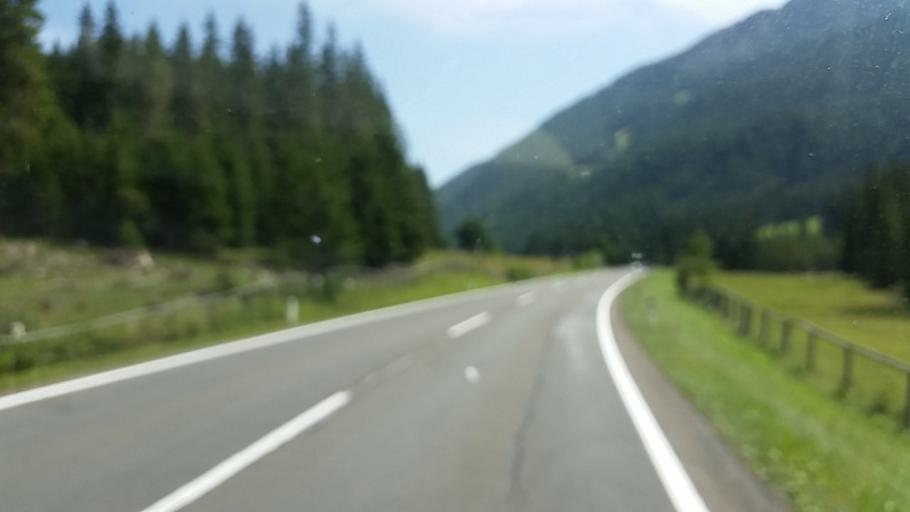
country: AT
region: Salzburg
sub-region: Politischer Bezirk Tamsweg
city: Mauterndorf
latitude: 47.1562
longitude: 13.6531
